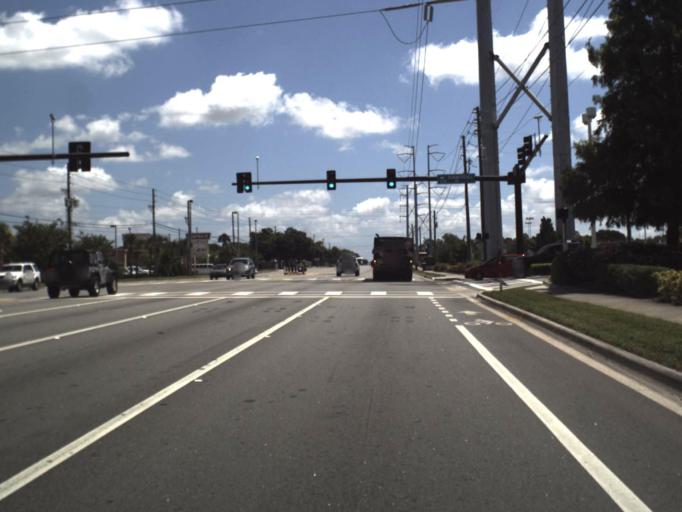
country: US
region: Florida
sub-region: Pinellas County
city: Dunedin
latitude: 28.0193
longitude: -82.7344
